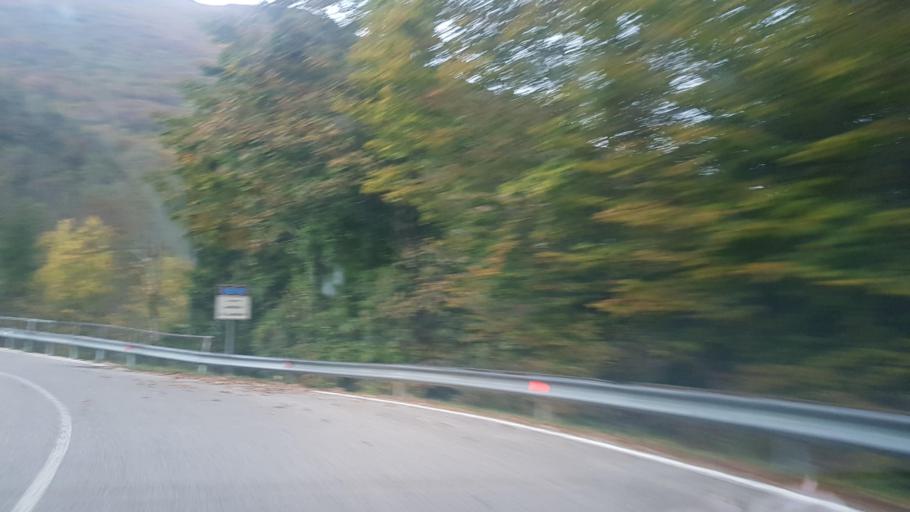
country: IT
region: Friuli Venezia Giulia
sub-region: Provincia di Udine
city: Chiaulis
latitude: 46.3846
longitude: 12.9644
